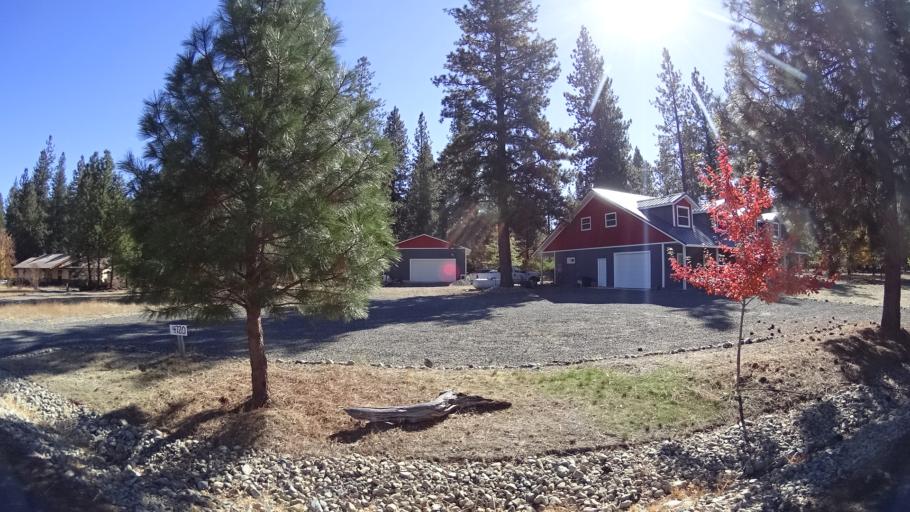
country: US
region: California
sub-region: Siskiyou County
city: Yreka
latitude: 41.5236
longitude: -122.9210
